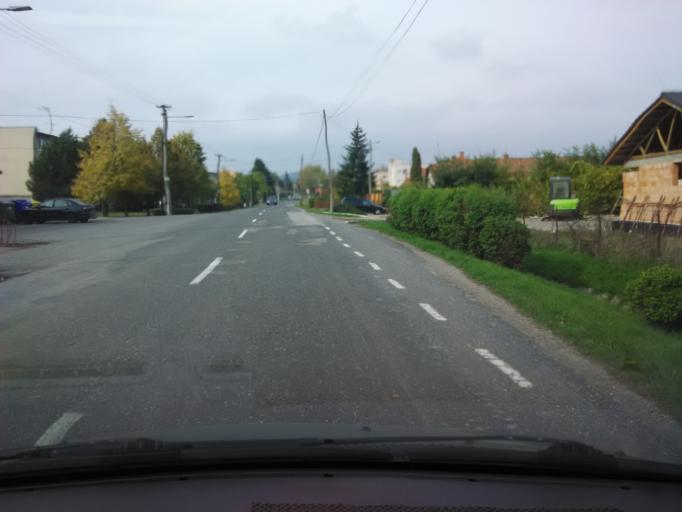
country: SK
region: Nitriansky
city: Tlmace
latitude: 48.2473
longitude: 18.5177
